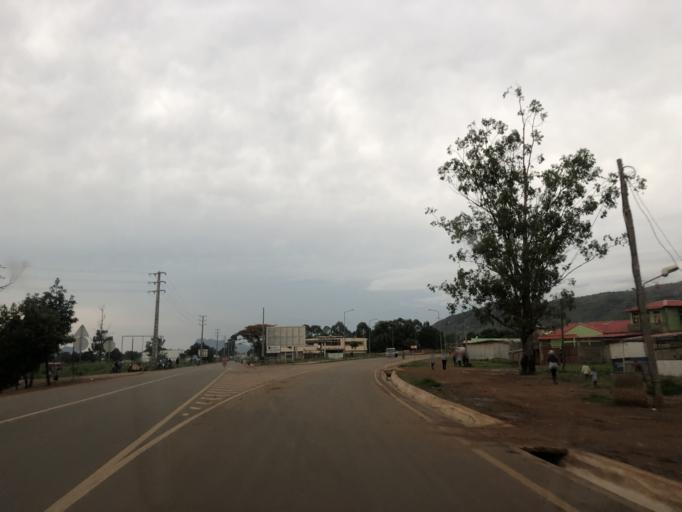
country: AO
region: Cuanza Sul
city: Uacu Cungo
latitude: -11.3546
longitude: 15.1212
